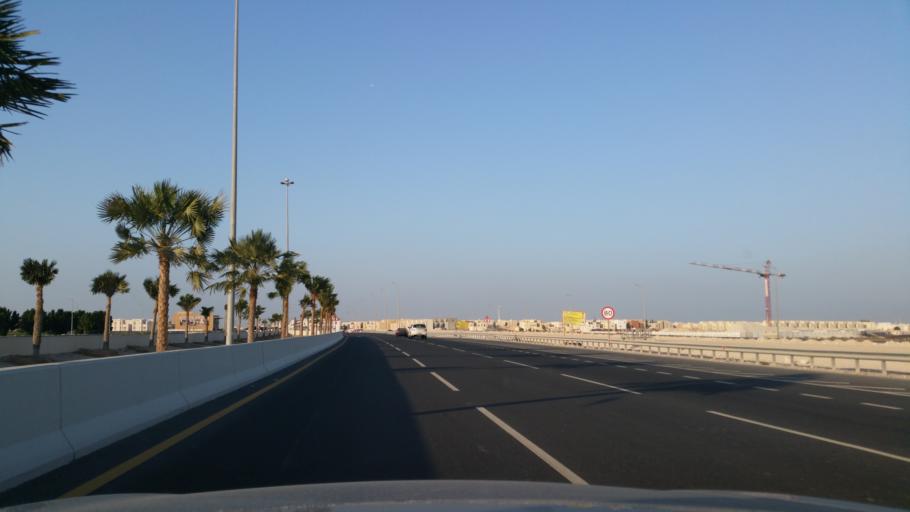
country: QA
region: Al Khawr
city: Al Khawr
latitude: 25.6597
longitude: 51.5004
